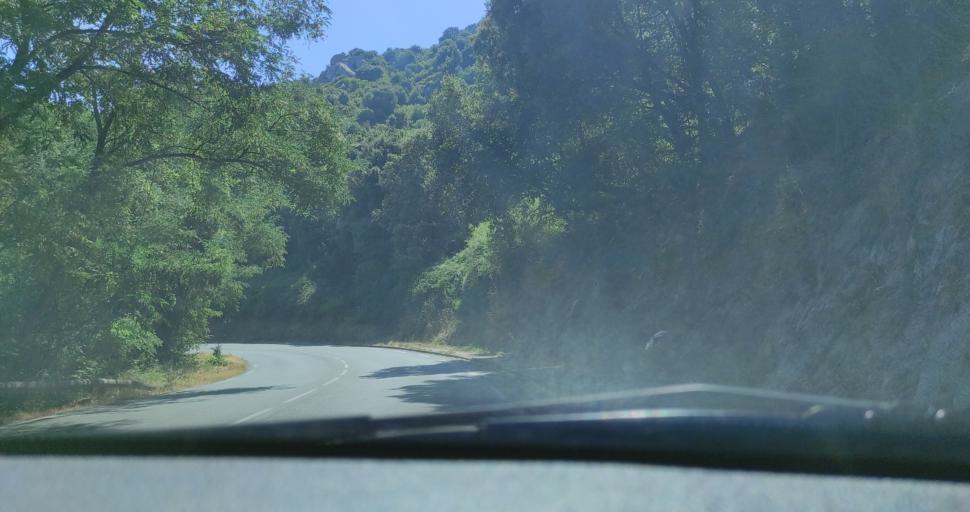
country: FR
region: Corsica
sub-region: Departement de la Corse-du-Sud
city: Sartene
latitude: 41.6165
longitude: 8.9579
